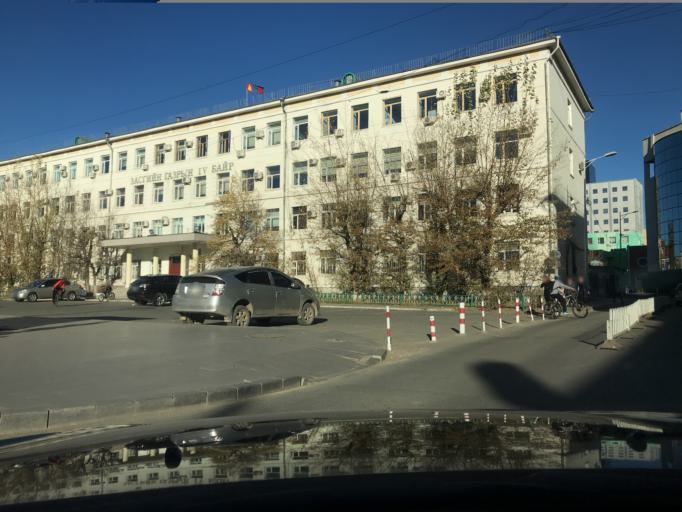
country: MN
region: Ulaanbaatar
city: Ulaanbaatar
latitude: 47.9179
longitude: 106.9119
